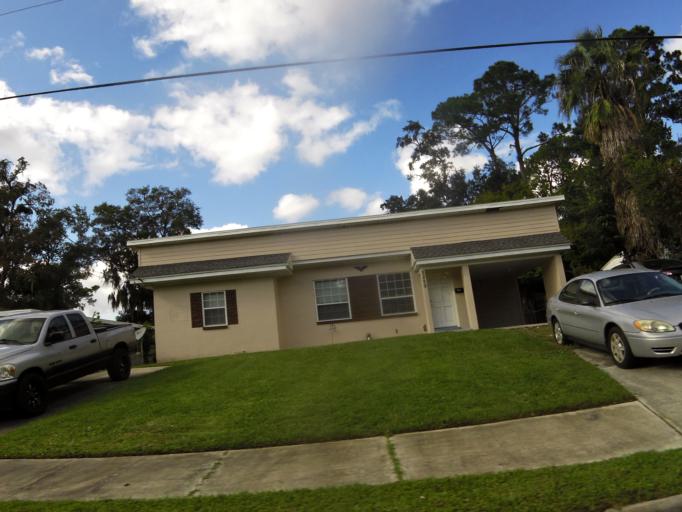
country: US
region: Florida
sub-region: Duval County
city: Jacksonville
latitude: 30.2865
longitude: -81.7354
